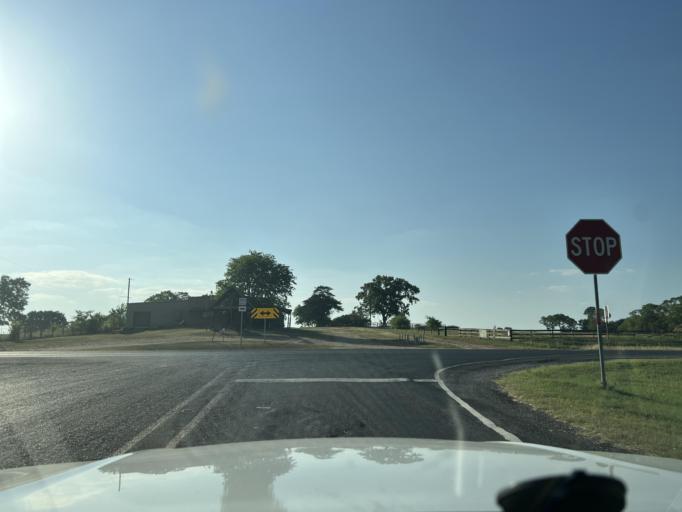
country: US
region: Texas
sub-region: Washington County
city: Brenham
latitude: 30.2356
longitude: -96.2851
